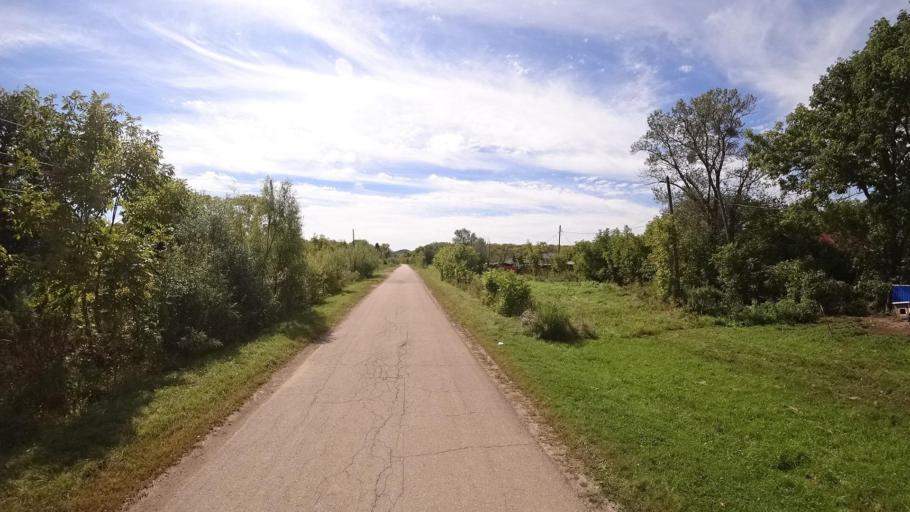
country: RU
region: Primorskiy
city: Yakovlevka
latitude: 44.7529
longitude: 133.6064
